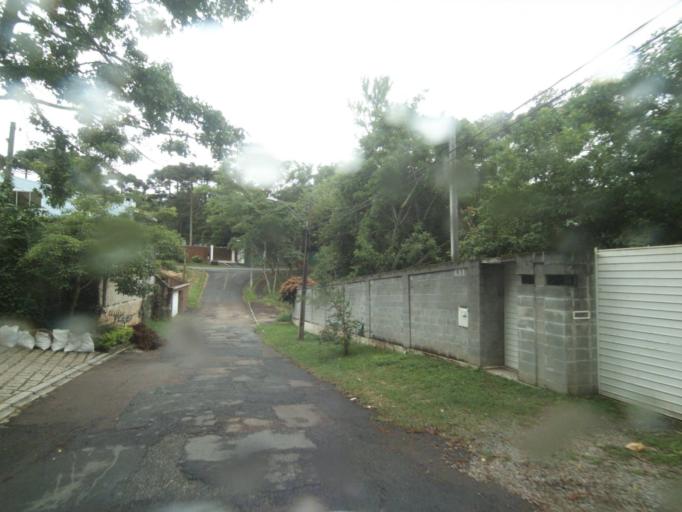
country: BR
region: Parana
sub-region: Curitiba
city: Curitiba
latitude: -25.4220
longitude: -49.3223
